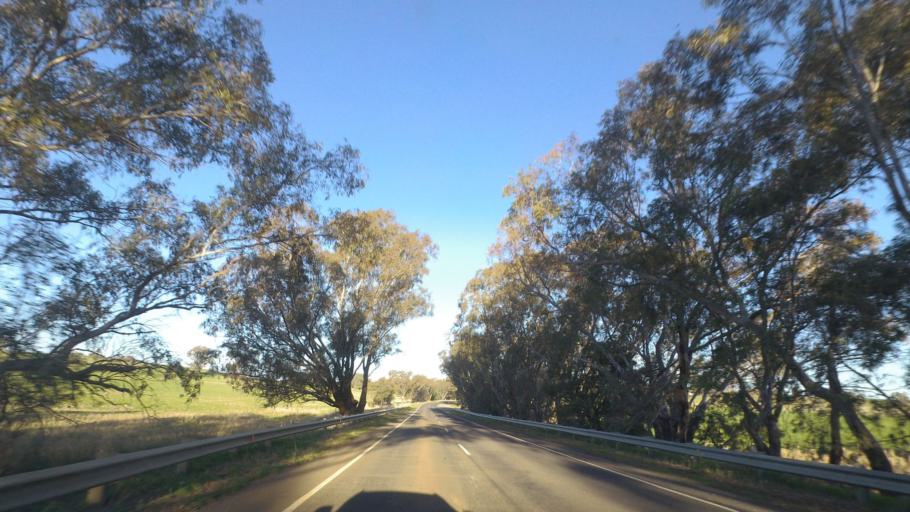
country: AU
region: Victoria
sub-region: Mount Alexander
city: Castlemaine
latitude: -37.0942
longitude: 144.5089
